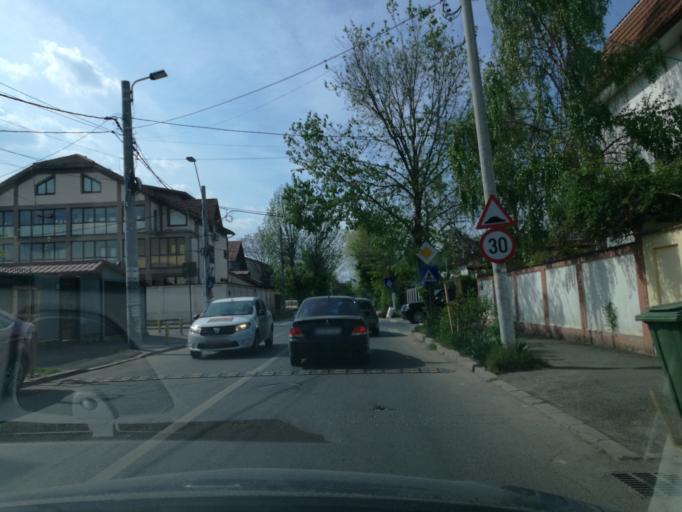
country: RO
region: Ilfov
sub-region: Comuna Chiajna
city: Rosu
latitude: 44.4432
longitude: 26.0283
